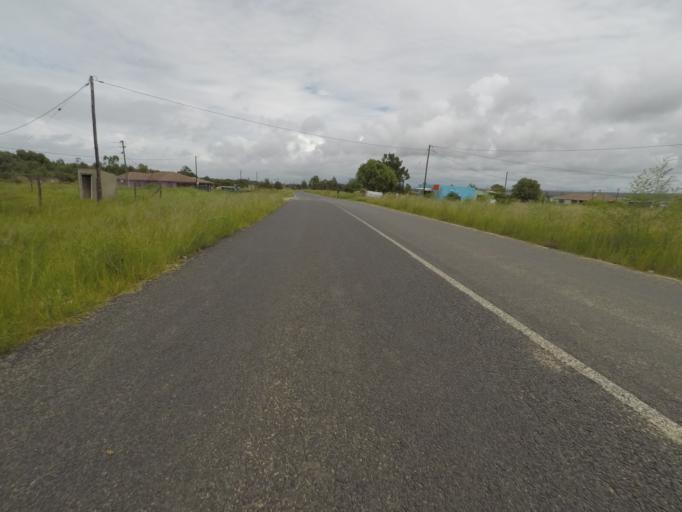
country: ZA
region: KwaZulu-Natal
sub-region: uThungulu District Municipality
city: eSikhawini
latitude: -28.9099
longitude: 31.8738
